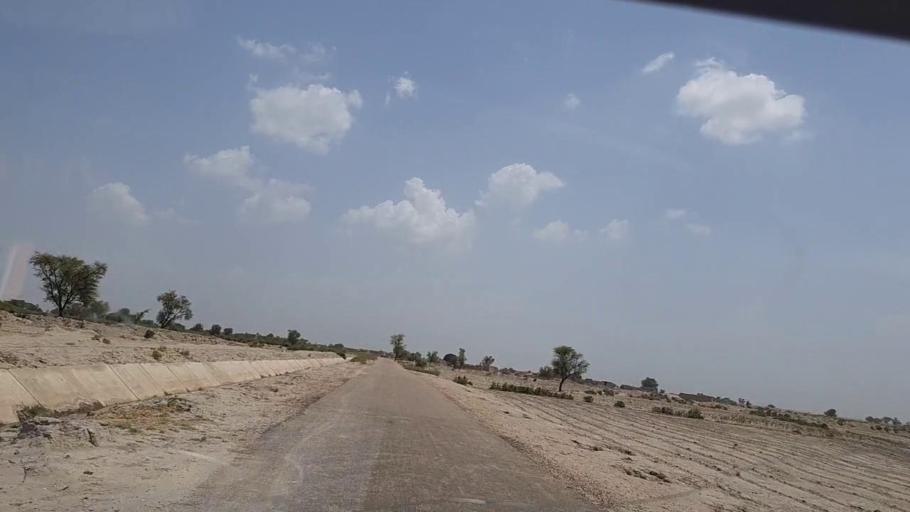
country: PK
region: Sindh
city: Bhan
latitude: 26.5271
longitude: 67.6339
